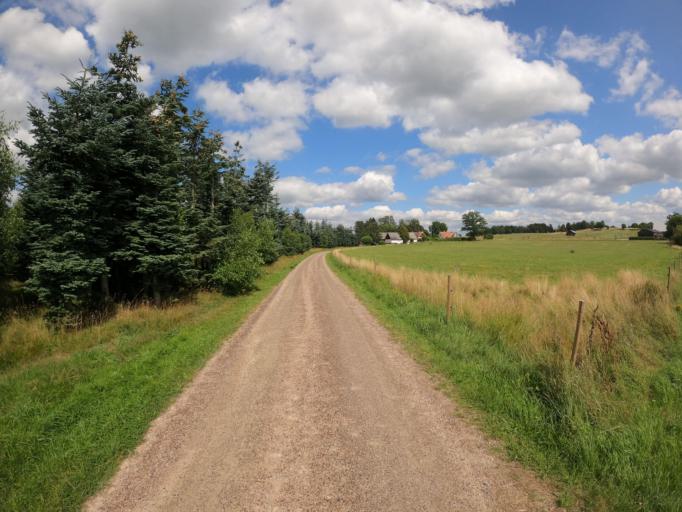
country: SE
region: Skane
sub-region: Lunds Kommun
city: Veberod
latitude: 55.6004
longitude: 13.4867
